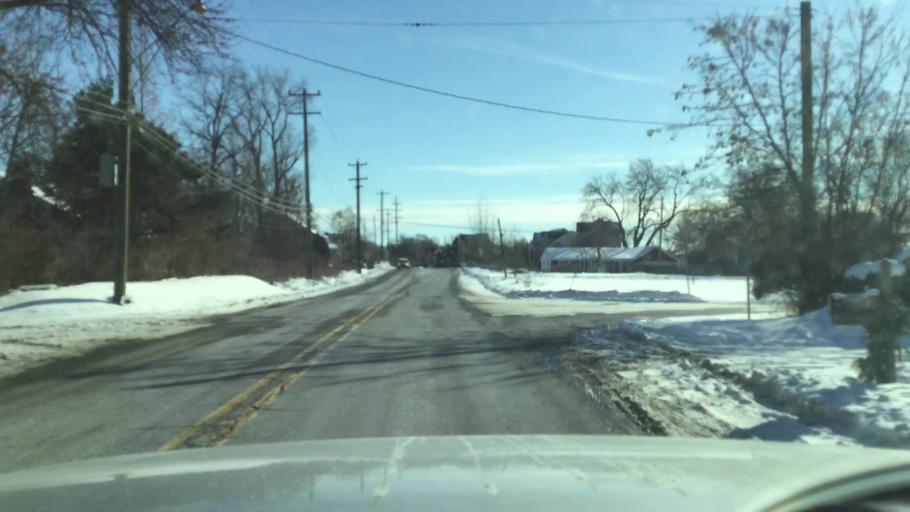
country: US
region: Michigan
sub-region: Oakland County
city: Keego Harbor
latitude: 42.6192
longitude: -83.3515
